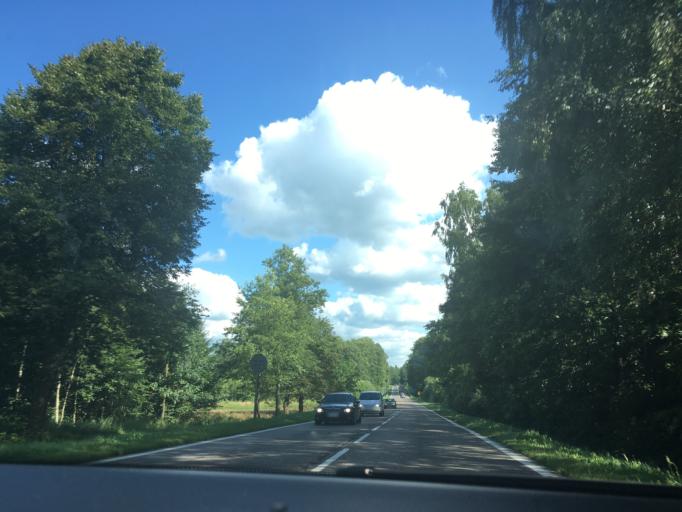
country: PL
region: Podlasie
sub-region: Powiat bialostocki
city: Wasilkow
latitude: 53.3283
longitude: 23.1178
